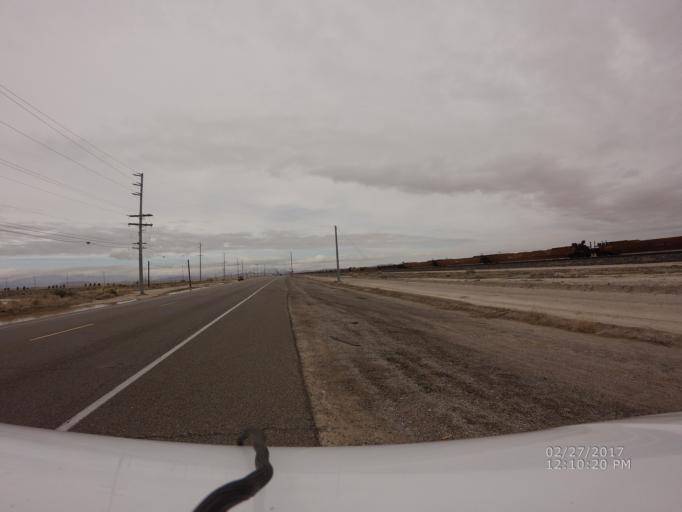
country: US
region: California
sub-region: Los Angeles County
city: Lancaster
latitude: 34.7741
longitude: -118.1487
